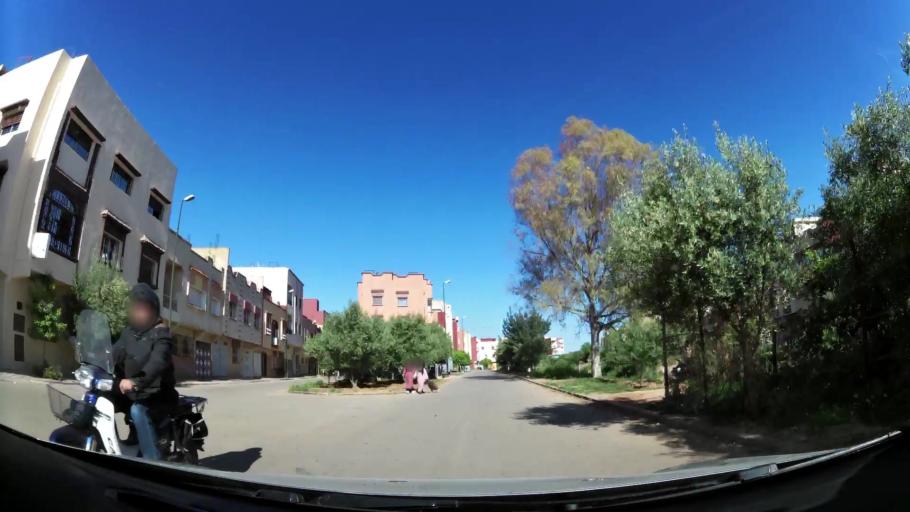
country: MA
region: Meknes-Tafilalet
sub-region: Meknes
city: Meknes
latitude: 33.8870
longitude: -5.5020
